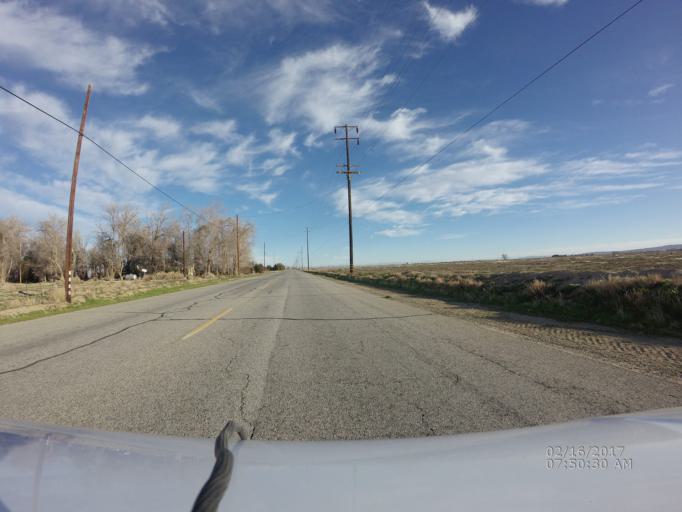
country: US
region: California
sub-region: Los Angeles County
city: Lancaster
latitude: 34.7153
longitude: -117.9697
